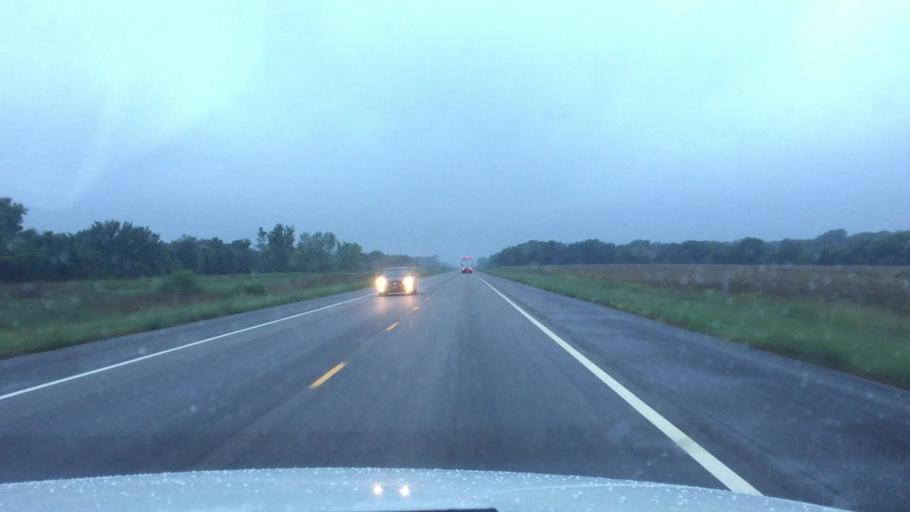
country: US
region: Kansas
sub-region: Montgomery County
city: Cherryvale
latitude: 37.4395
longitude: -95.4863
